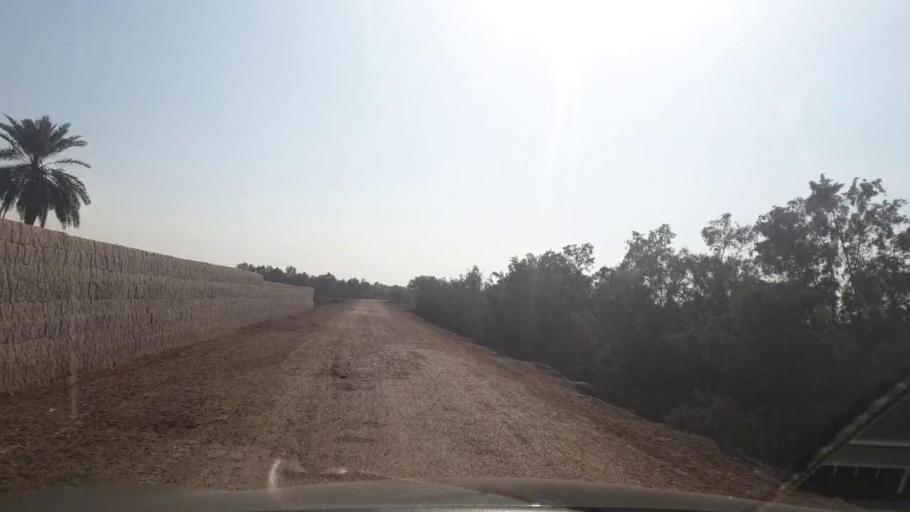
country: PK
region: Sindh
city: Khairpur
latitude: 28.1420
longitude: 69.6025
